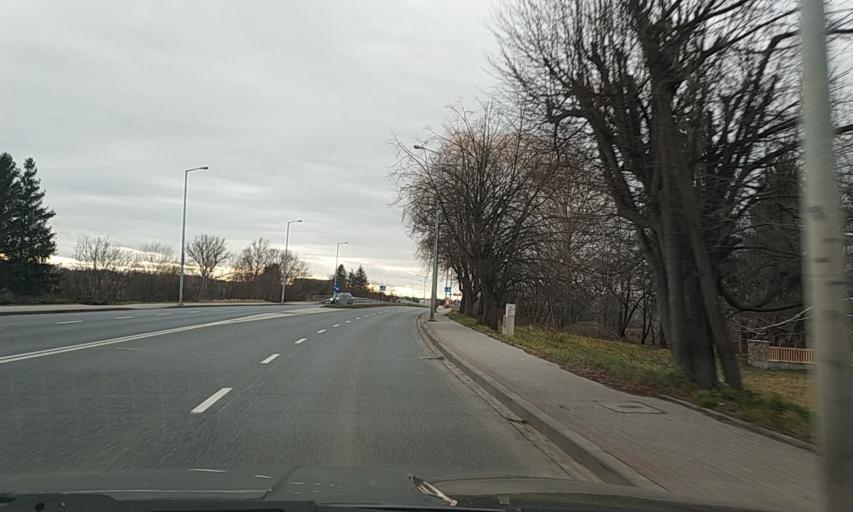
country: PL
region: Lesser Poland Voivodeship
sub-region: Powiat tarnowski
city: Koszyce Wielkie
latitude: 49.9978
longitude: 20.9520
